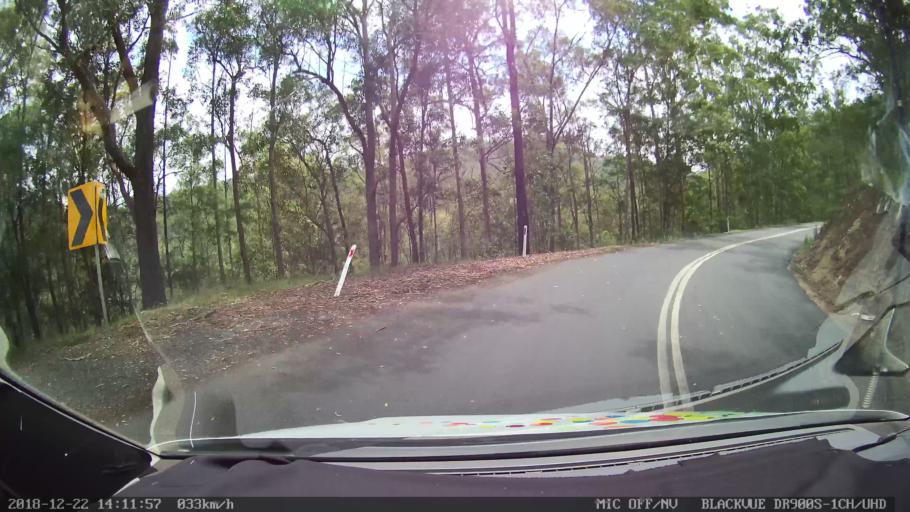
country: AU
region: New South Wales
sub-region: Clarence Valley
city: Coutts Crossing
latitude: -29.9999
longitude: 152.7088
